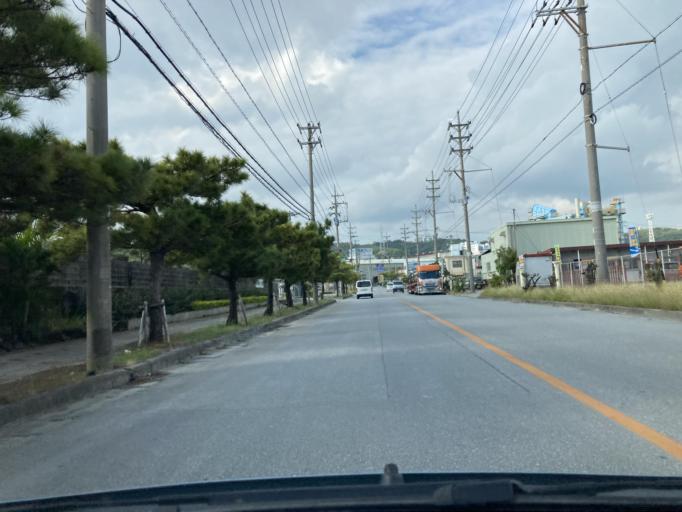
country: JP
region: Okinawa
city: Ginowan
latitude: 26.2292
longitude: 127.7746
